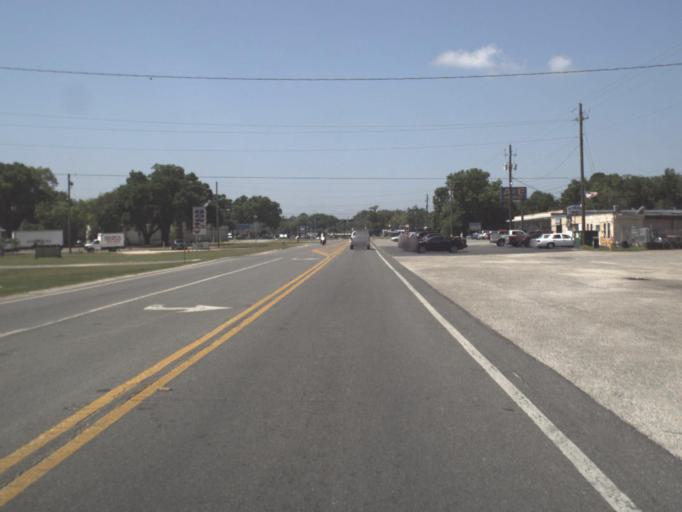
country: US
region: Florida
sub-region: Escambia County
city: West Pensacola
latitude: 30.4259
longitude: -87.2716
